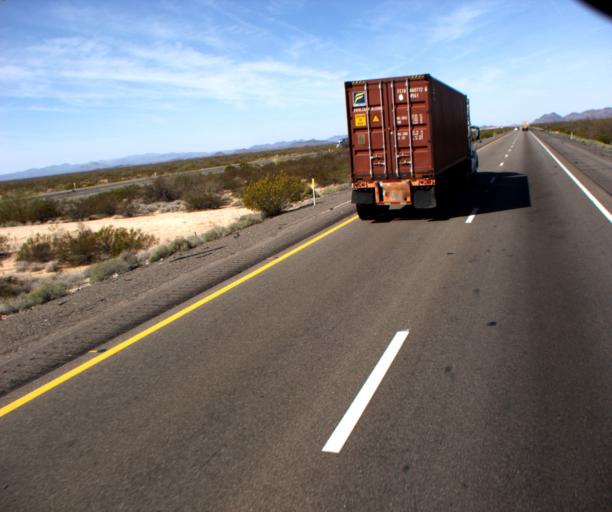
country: US
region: Arizona
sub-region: La Paz County
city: Salome
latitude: 33.5910
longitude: -113.4969
